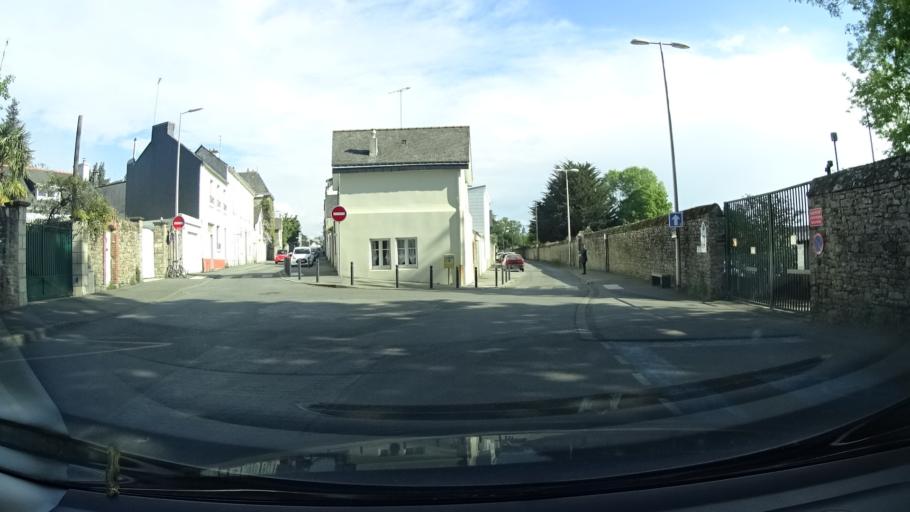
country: FR
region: Brittany
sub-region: Departement du Morbihan
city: Vannes
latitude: 47.6520
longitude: -2.7644
